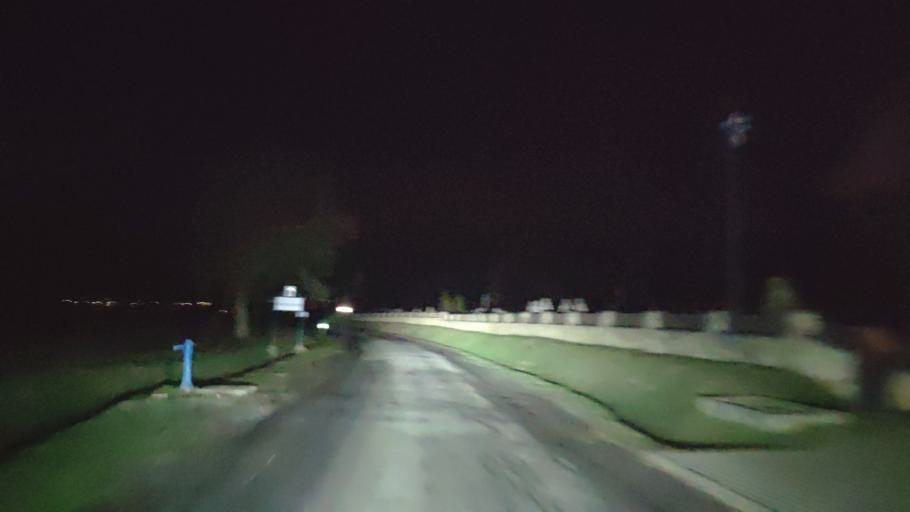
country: HU
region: Borsod-Abauj-Zemplen
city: Satoraljaujhely
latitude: 48.4692
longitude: 21.6168
